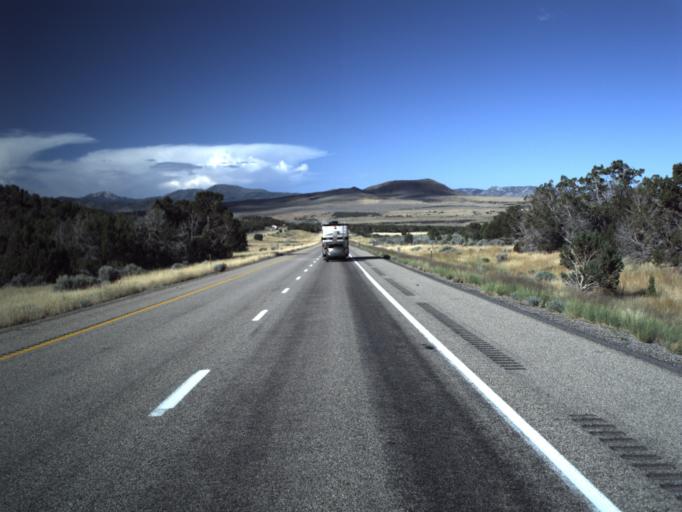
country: US
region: Utah
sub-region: Beaver County
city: Beaver
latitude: 38.6014
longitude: -112.5569
